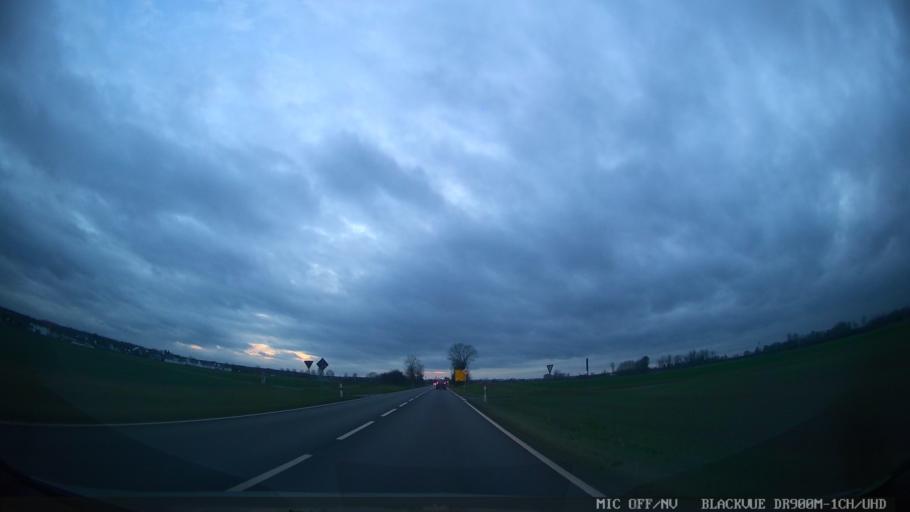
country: DE
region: Hesse
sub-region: Regierungsbezirk Darmstadt
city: Munster
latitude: 49.9323
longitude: 8.9123
